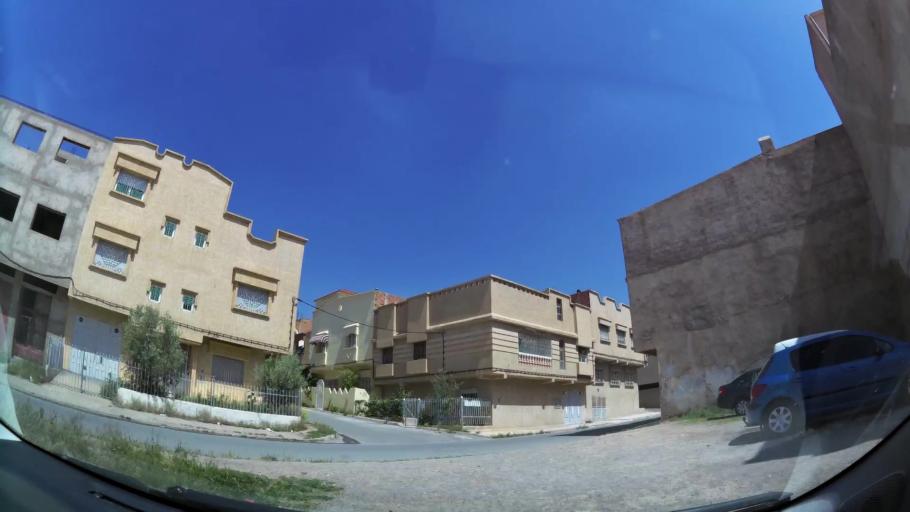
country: MA
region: Oriental
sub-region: Oujda-Angad
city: Oujda
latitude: 34.6894
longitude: -1.8811
